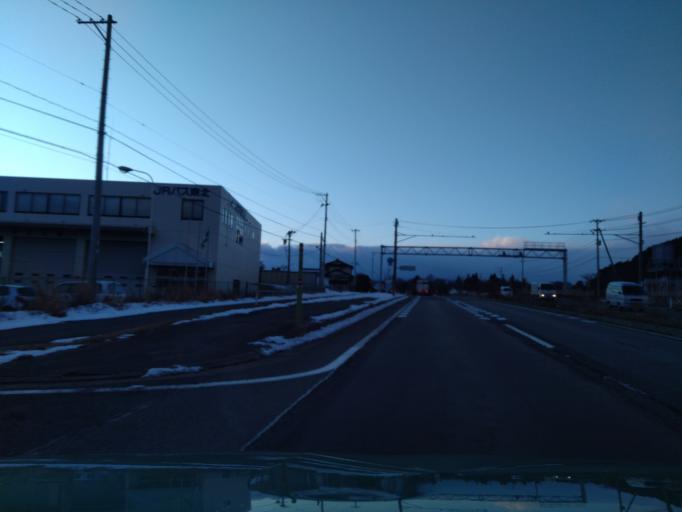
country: JP
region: Iwate
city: Shizukuishi
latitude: 39.7009
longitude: 141.0506
